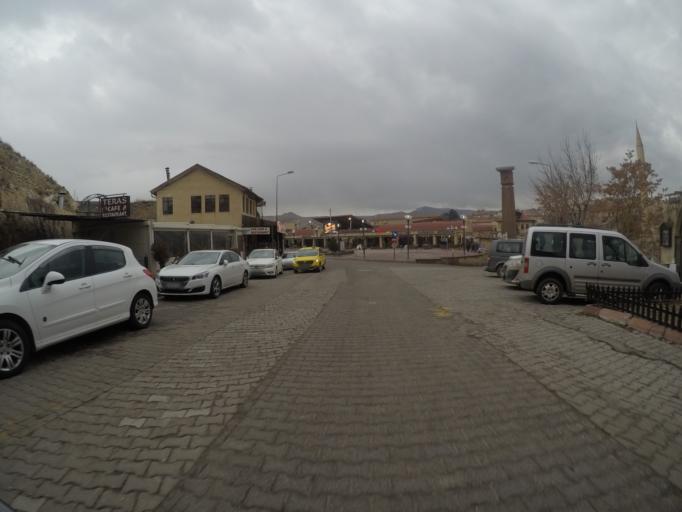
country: TR
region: Nevsehir
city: Urgub
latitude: 38.6307
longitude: 34.9100
